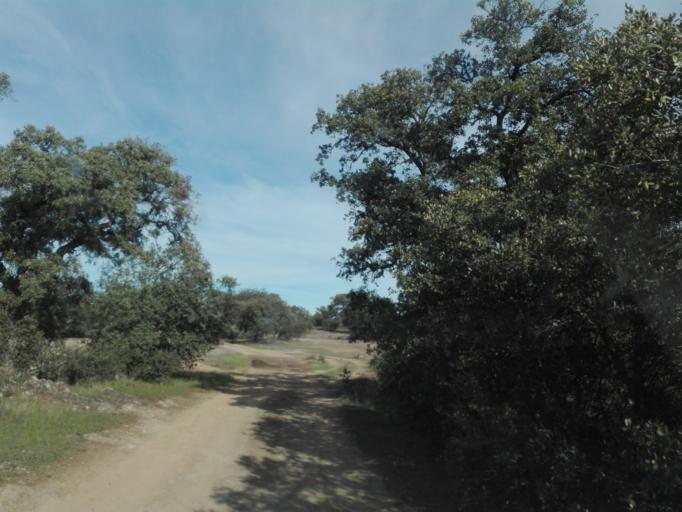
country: ES
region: Extremadura
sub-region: Provincia de Badajoz
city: Azuaga
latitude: 38.2262
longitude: -5.7396
